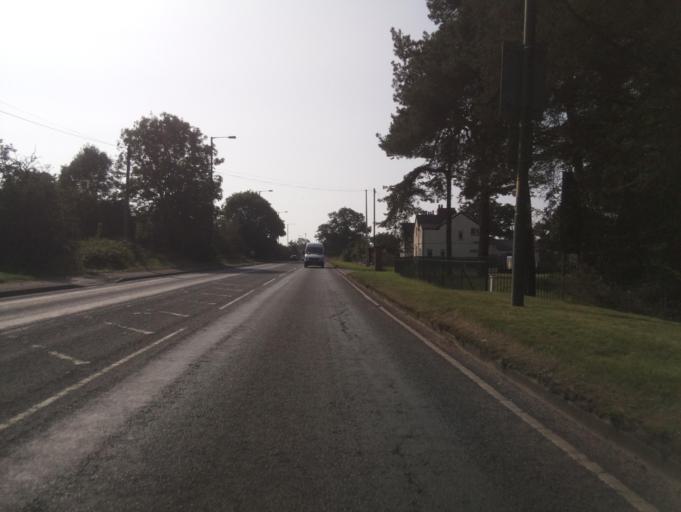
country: GB
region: England
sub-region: Walsall
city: Streetly
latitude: 52.5966
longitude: -1.8915
